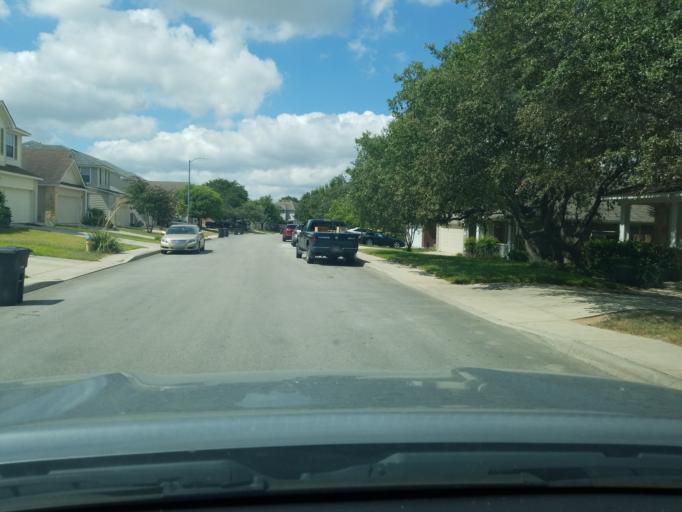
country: US
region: Texas
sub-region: Bexar County
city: Timberwood Park
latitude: 29.6593
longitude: -98.4951
